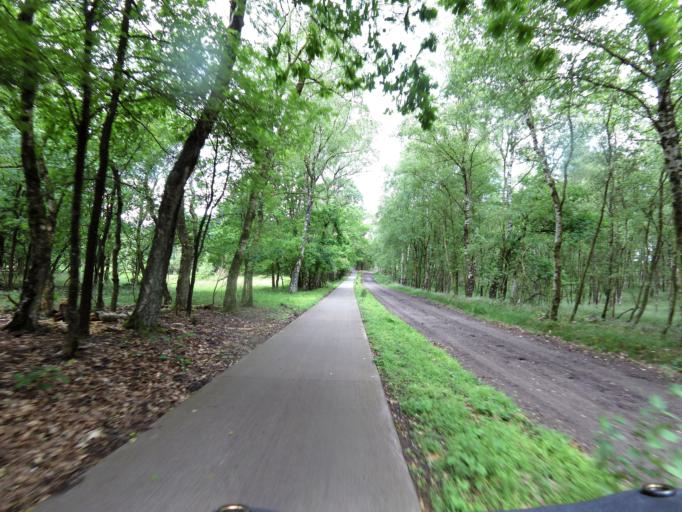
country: NL
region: Gelderland
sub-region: Gemeente Apeldoorn
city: Uddel
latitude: 52.3157
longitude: 5.7612
